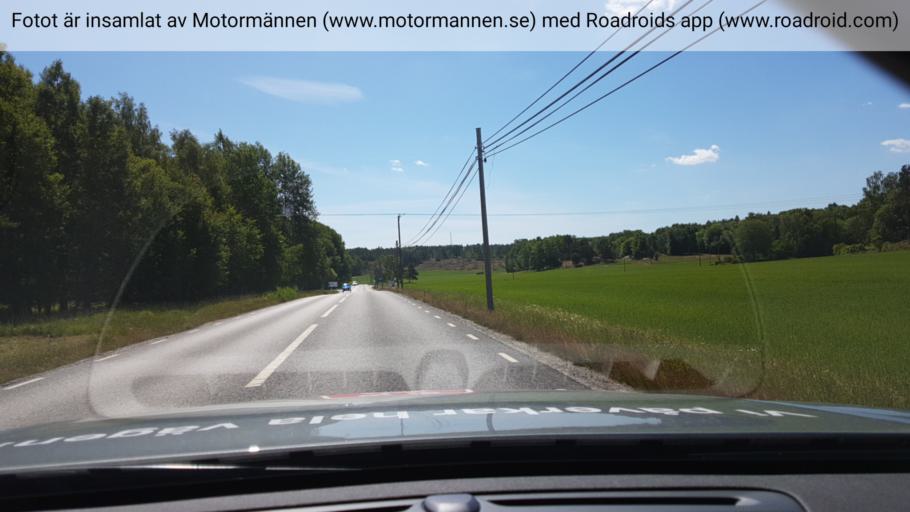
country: SE
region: Stockholm
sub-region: Haninge Kommun
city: Haninge
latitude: 59.1363
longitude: 18.1880
